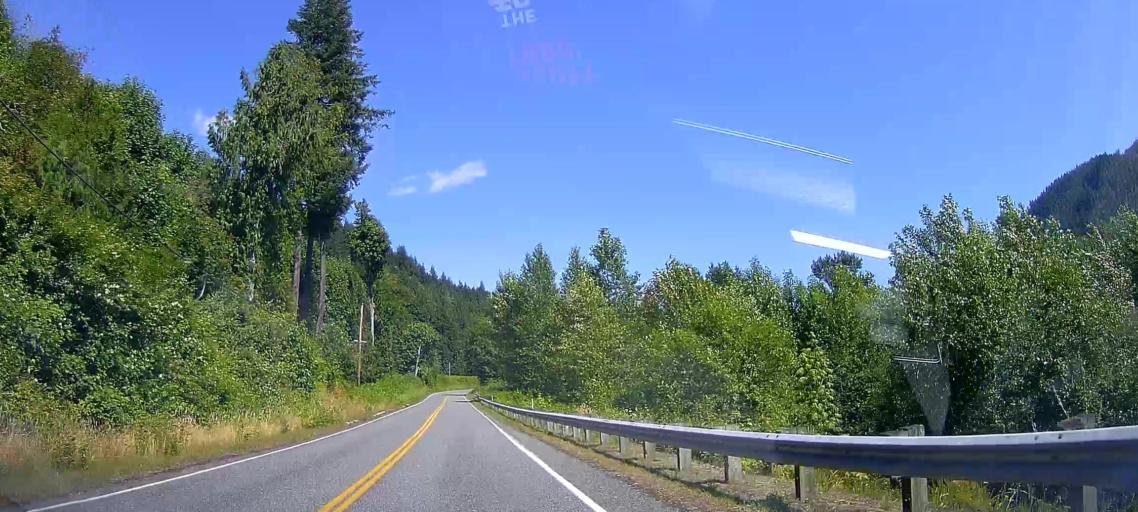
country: US
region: Washington
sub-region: Whatcom County
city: Sudden Valley
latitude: 48.6738
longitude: -122.2625
